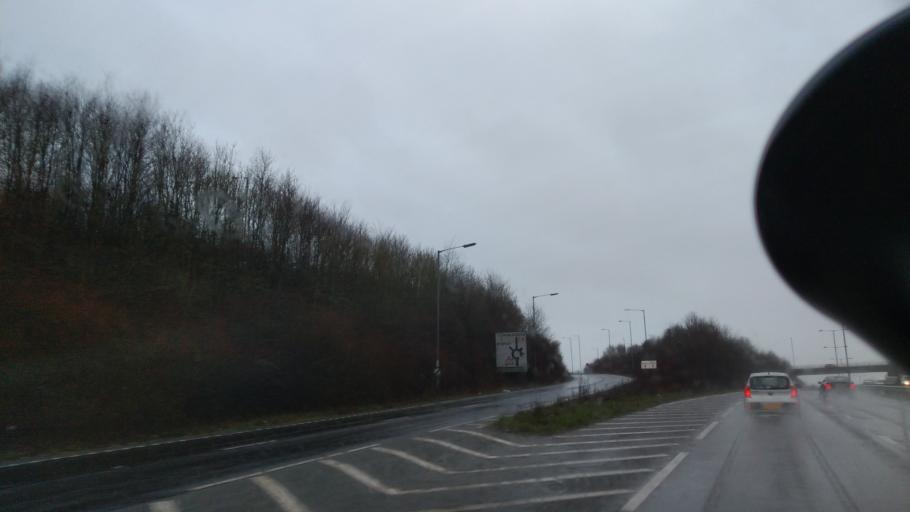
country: GB
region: England
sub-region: Brighton and Hove
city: Hove
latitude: 50.8602
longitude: -0.1737
